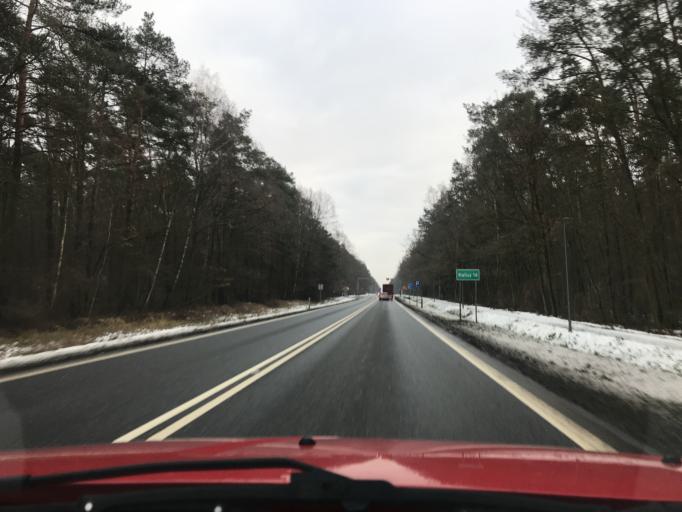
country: PL
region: Greater Poland Voivodeship
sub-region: Powiat pleszewski
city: Goluchow
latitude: 51.8460
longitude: 17.9393
